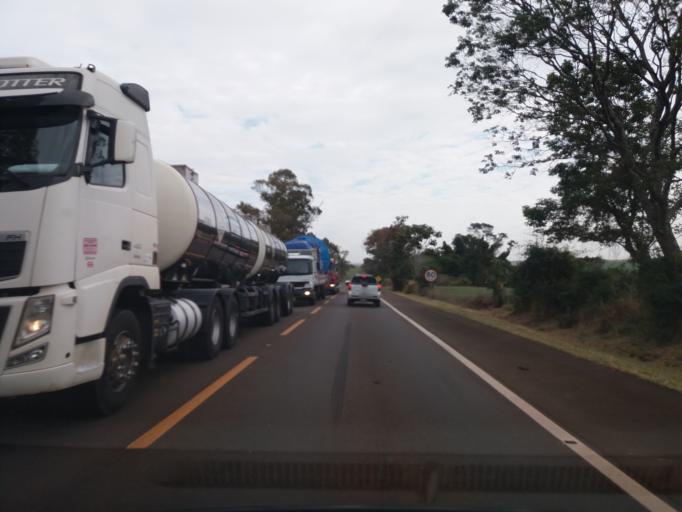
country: BR
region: Parana
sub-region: Campo Mourao
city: Campo Mourao
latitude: -24.3167
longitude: -52.6226
